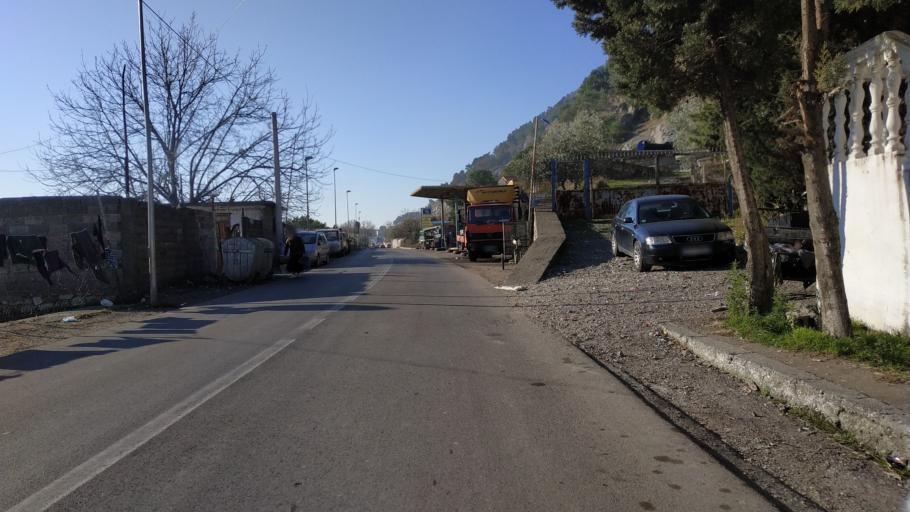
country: AL
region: Shkoder
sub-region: Rrethi i Shkodres
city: Shkoder
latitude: 42.0498
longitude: 19.4883
